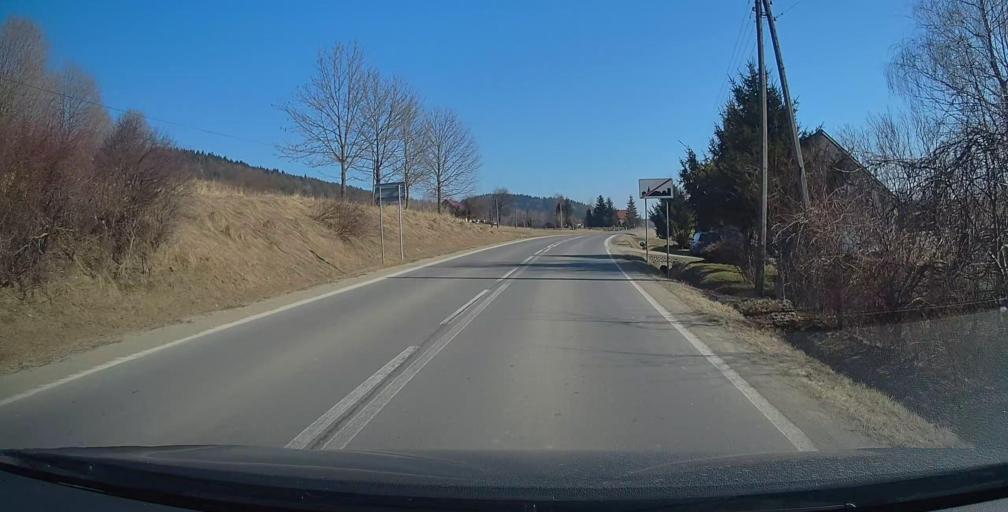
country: PL
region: Subcarpathian Voivodeship
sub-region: Powiat bieszczadzki
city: Ustrzyki Dolne
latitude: 49.4908
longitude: 22.6496
